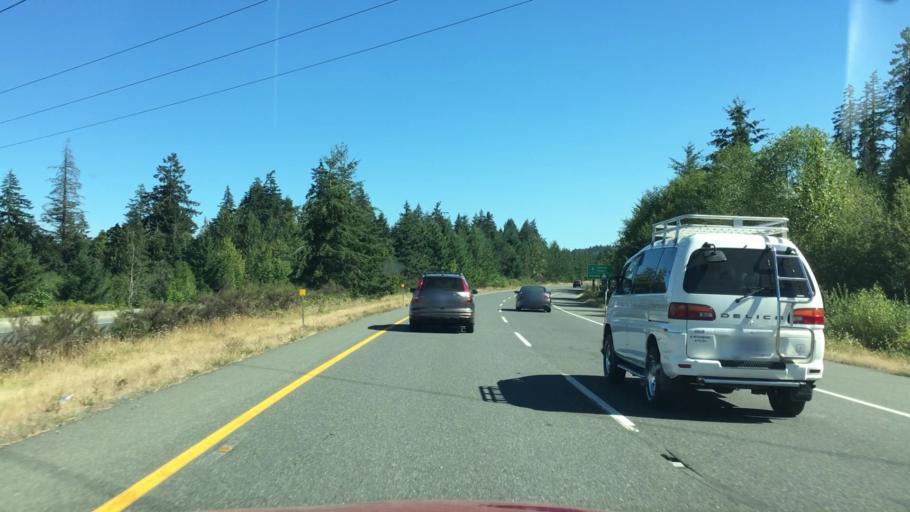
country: CA
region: British Columbia
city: Nanaimo
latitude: 49.1327
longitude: -123.9323
